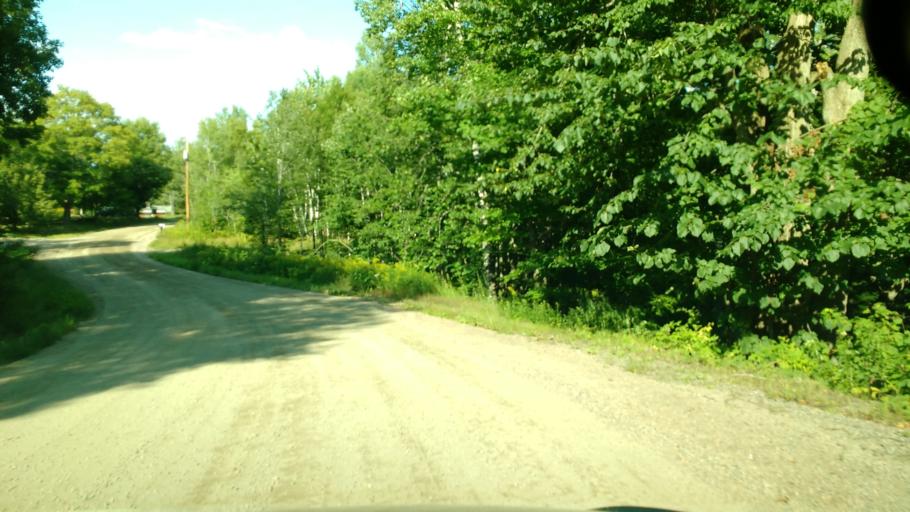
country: CA
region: Ontario
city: Powassan
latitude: 46.1808
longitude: -79.2988
